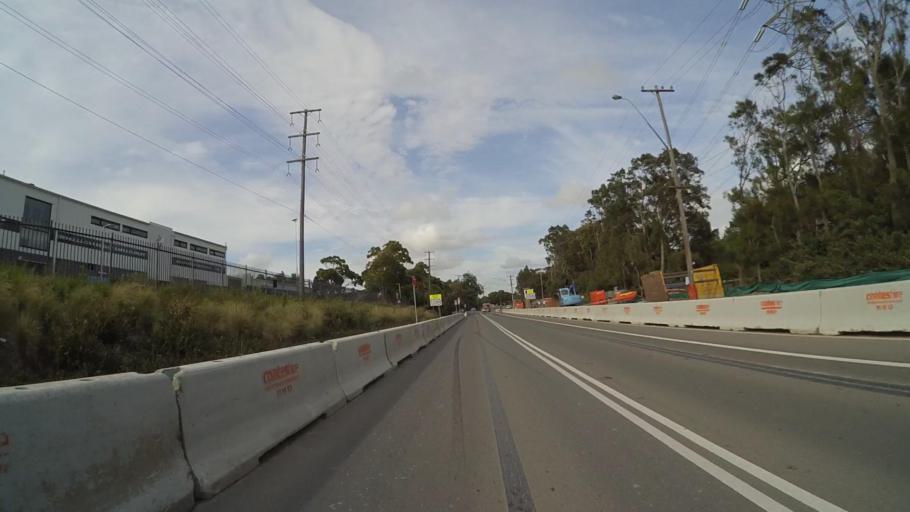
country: AU
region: New South Wales
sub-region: Sutherland Shire
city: Cronulla
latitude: -34.0373
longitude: 151.1590
